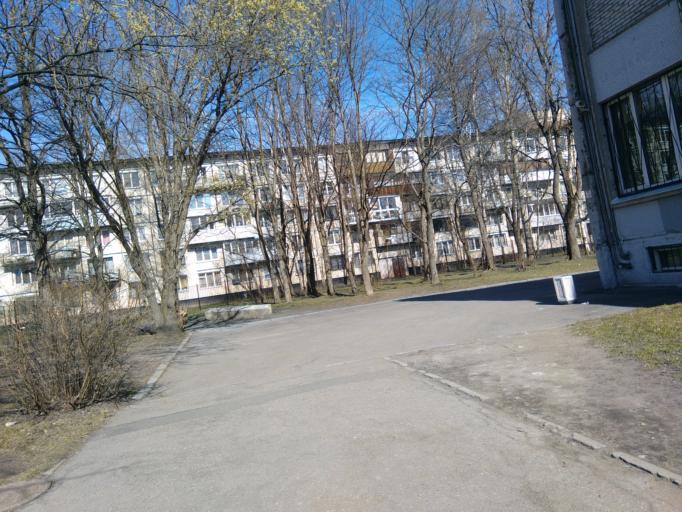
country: RU
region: St.-Petersburg
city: Grazhdanka
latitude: 60.0320
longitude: 30.4090
